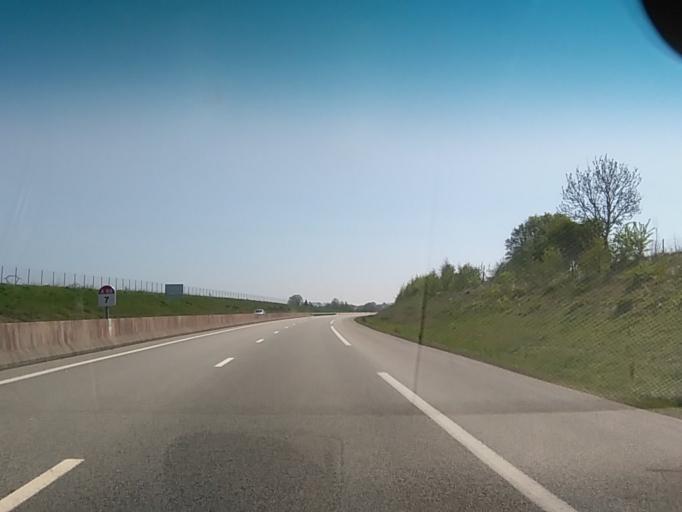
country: FR
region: Lower Normandy
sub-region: Departement de l'Orne
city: Mortree
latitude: 48.6566
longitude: 0.1066
